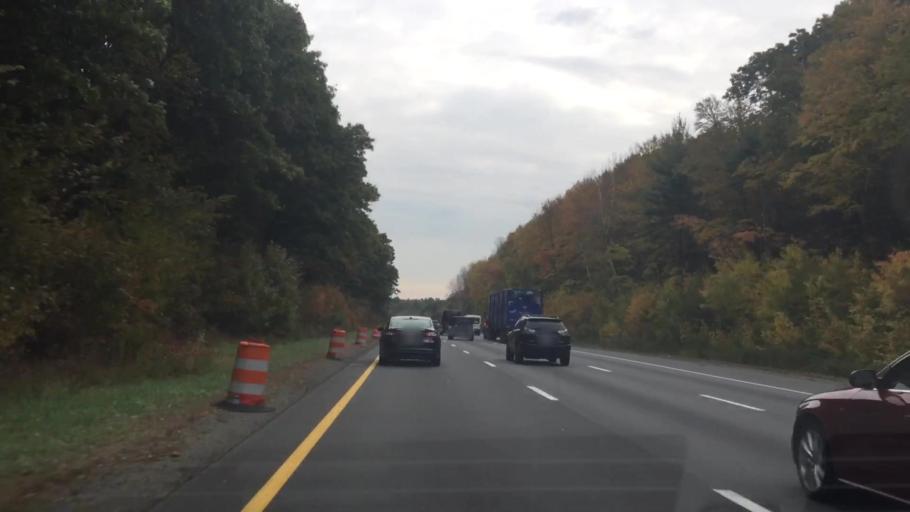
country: US
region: Massachusetts
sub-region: Middlesex County
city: Tewksbury
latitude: 42.6467
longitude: -71.2225
